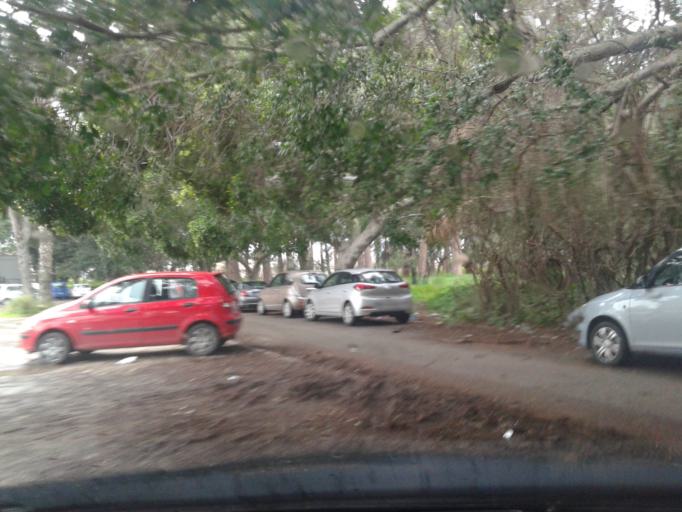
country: IT
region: Sicily
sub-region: Palermo
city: Monreale
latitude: 38.0926
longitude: 13.3120
